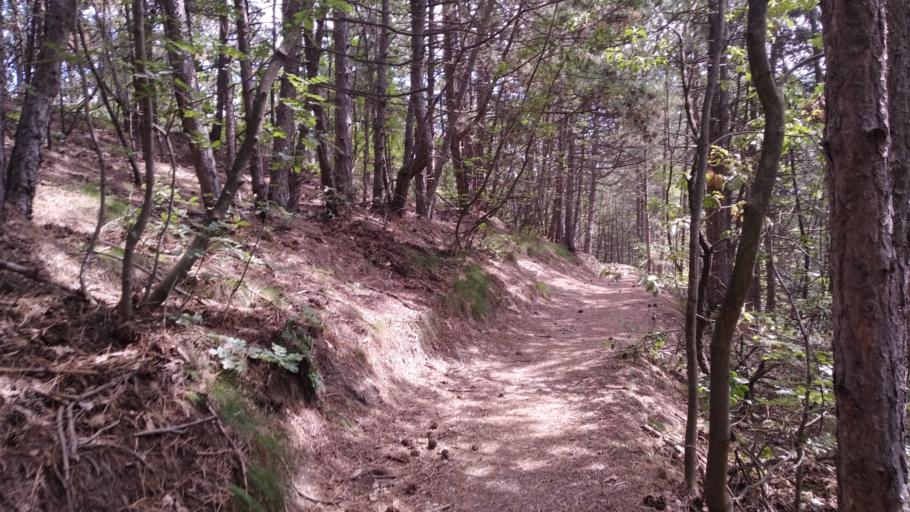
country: HU
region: Pest
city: Pilisszentivan
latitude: 47.6256
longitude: 18.8665
